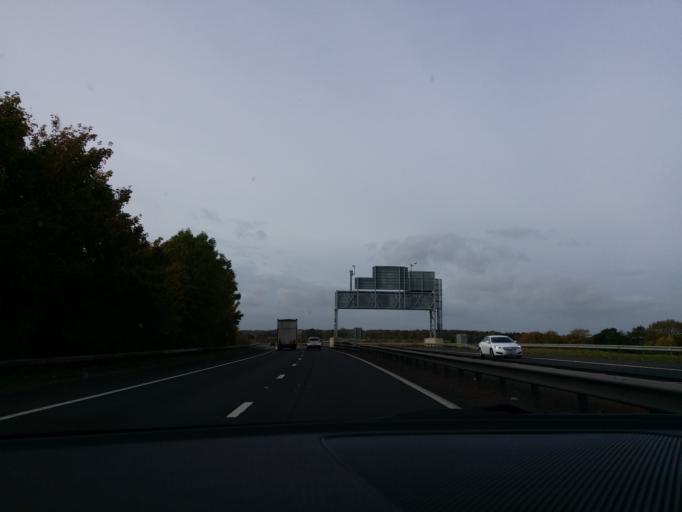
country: GB
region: Scotland
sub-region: West Lothian
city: Broxburn
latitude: 55.9656
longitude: -3.4472
